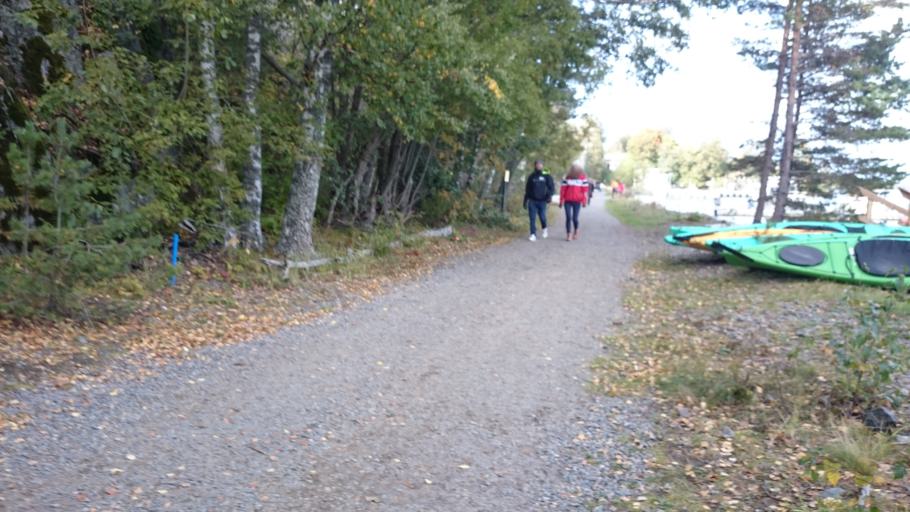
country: FI
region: Uusimaa
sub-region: Helsinki
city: Helsinki
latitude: 60.1356
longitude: 25.0097
